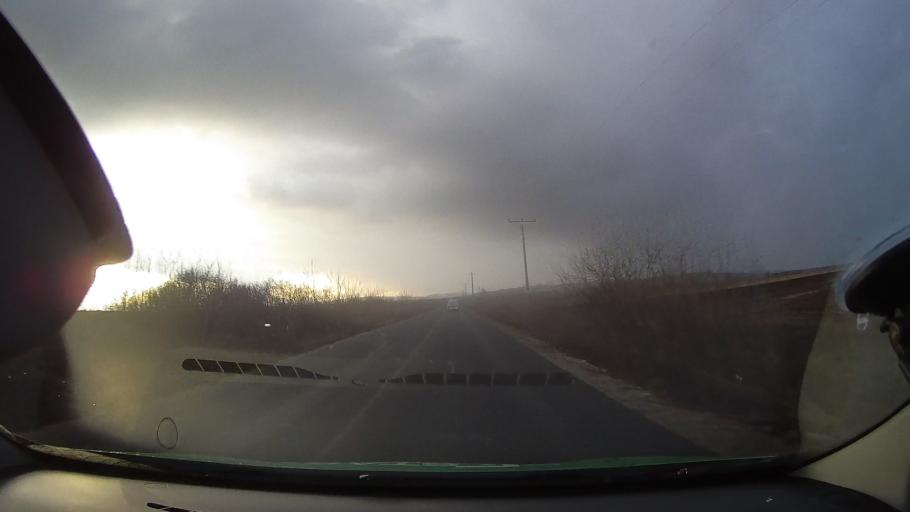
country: RO
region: Cluj
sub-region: Comuna Luna
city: Luncani
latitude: 46.4490
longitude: 23.9418
